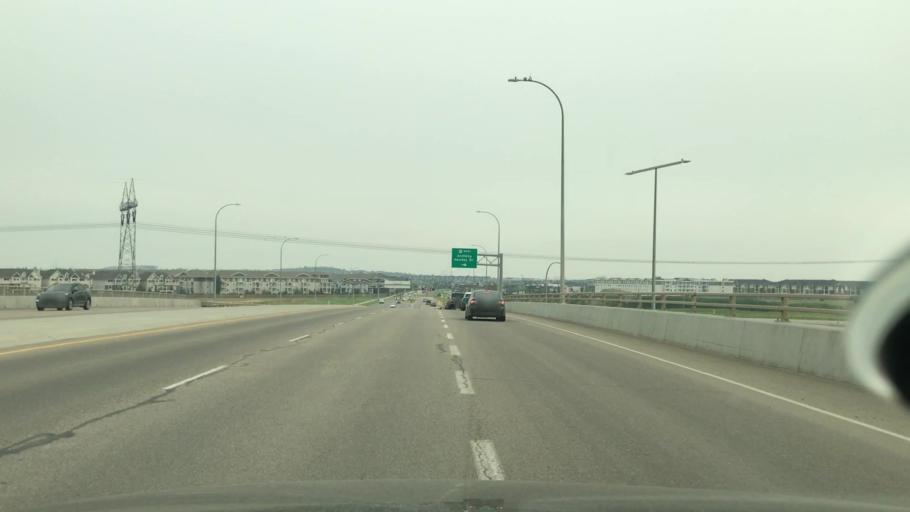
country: CA
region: Alberta
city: Devon
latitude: 53.4303
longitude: -113.5832
